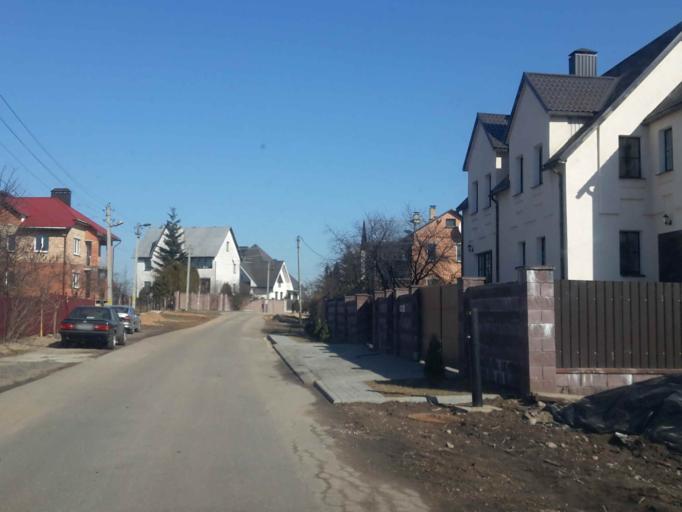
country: BY
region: Minsk
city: Zhdanovichy
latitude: 53.9177
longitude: 27.4005
